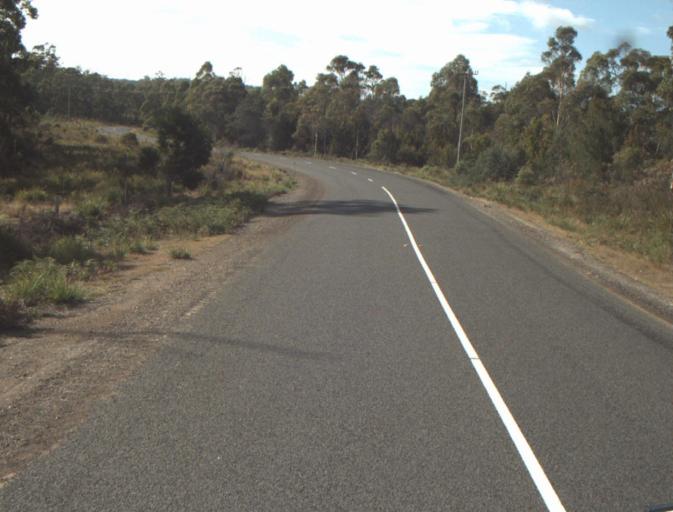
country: AU
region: Tasmania
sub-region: Dorset
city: Bridport
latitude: -41.1358
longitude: 147.2234
